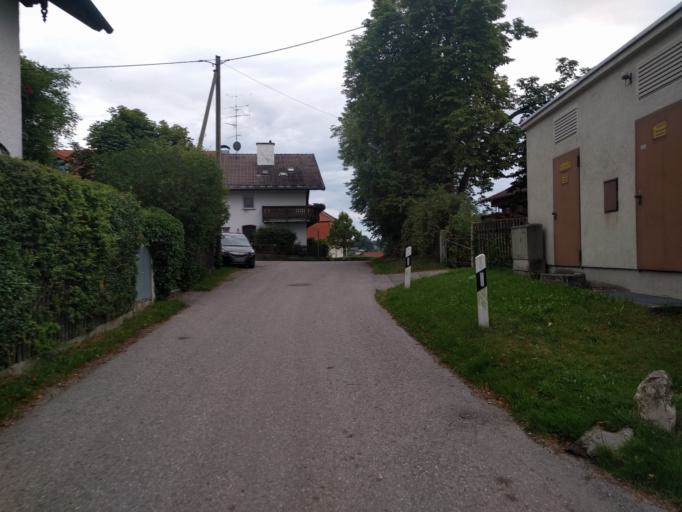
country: DE
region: Bavaria
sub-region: Upper Bavaria
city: Schaftlarn
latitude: 47.9931
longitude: 11.4532
